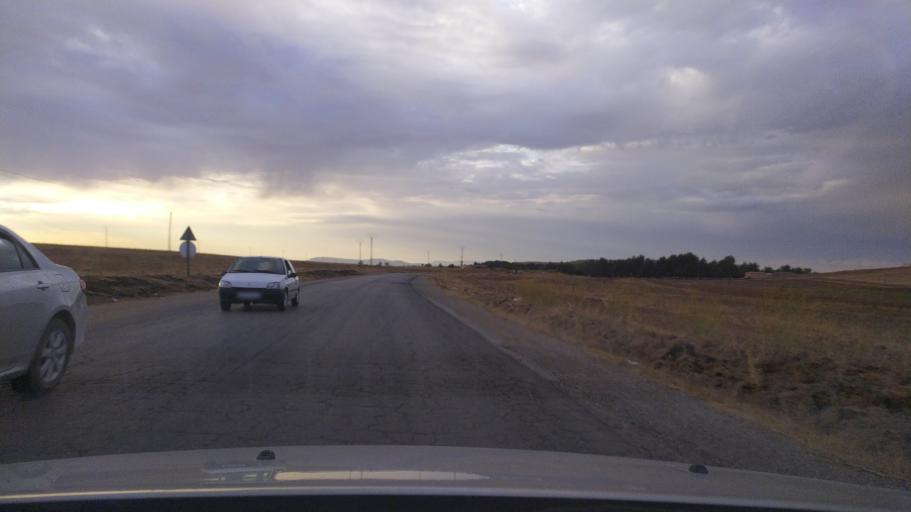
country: DZ
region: Tiaret
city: Frenda
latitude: 35.0277
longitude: 1.0968
